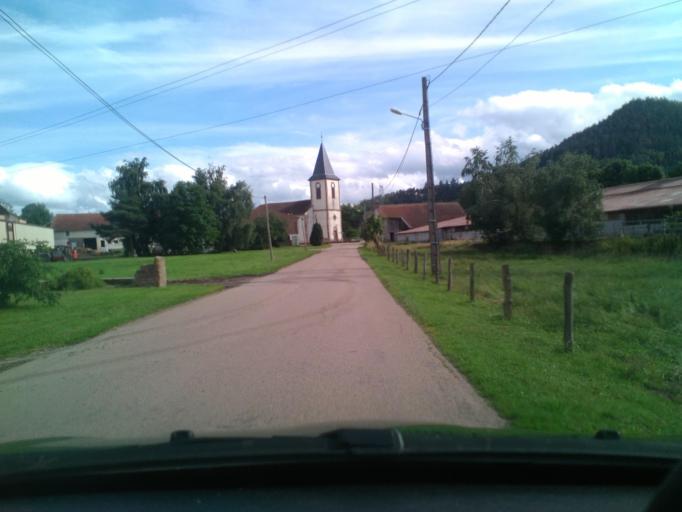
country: FR
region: Lorraine
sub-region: Departement des Vosges
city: Corcieux
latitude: 48.1970
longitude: 6.8532
